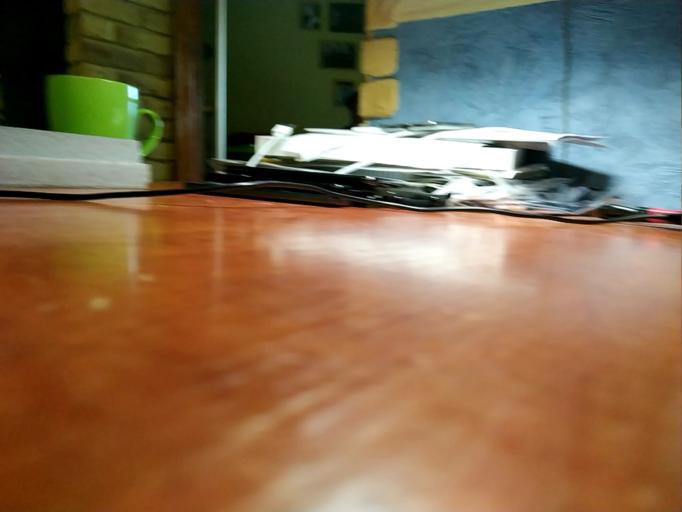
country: RU
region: Tverskaya
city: Staraya Toropa
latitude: 56.2423
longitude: 31.4046
